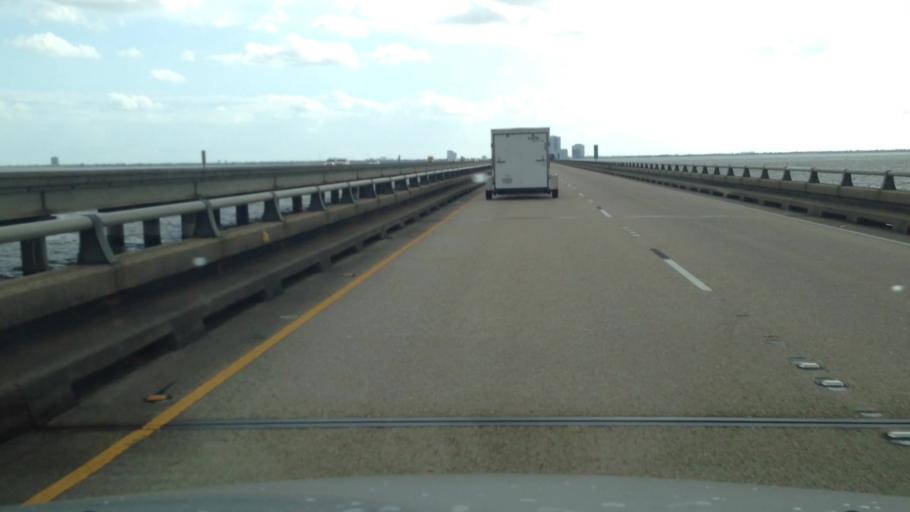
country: US
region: Louisiana
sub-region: Jefferson Parish
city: Metairie
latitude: 30.0628
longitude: -90.1469
